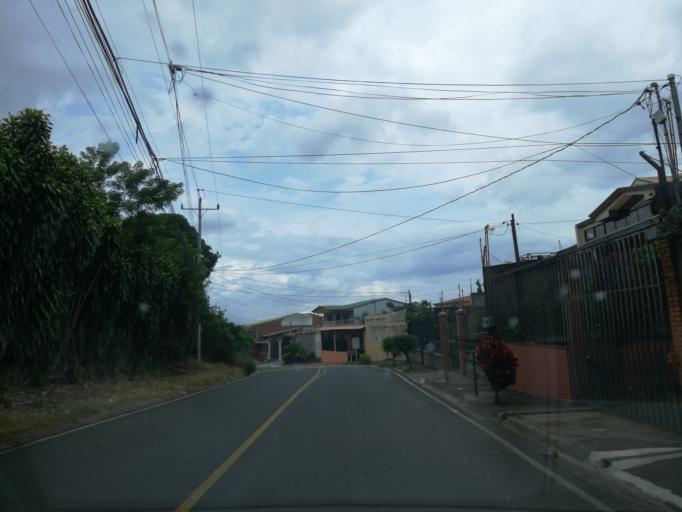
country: CR
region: Alajuela
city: Alajuela
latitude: 10.0294
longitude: -84.1957
